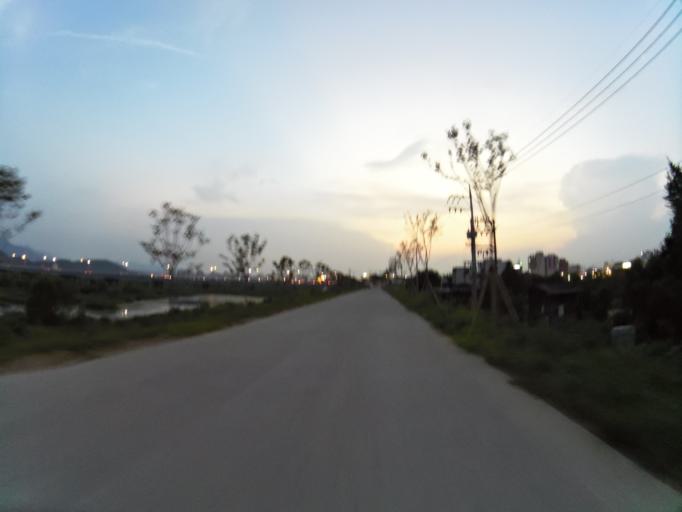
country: KR
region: Gyeongsangbuk-do
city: Gyeongsan-si
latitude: 35.8635
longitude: 128.7177
